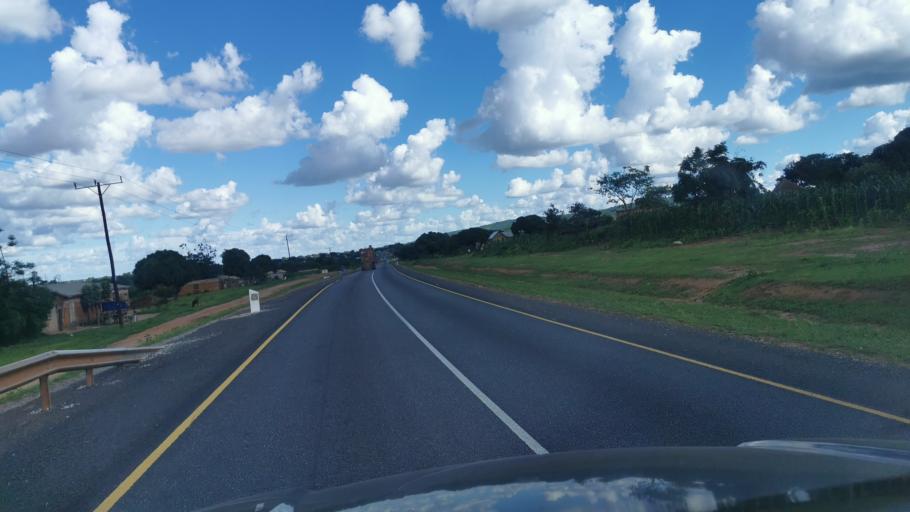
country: TZ
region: Geita
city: Ushirombo
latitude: -3.4361
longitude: 31.8338
